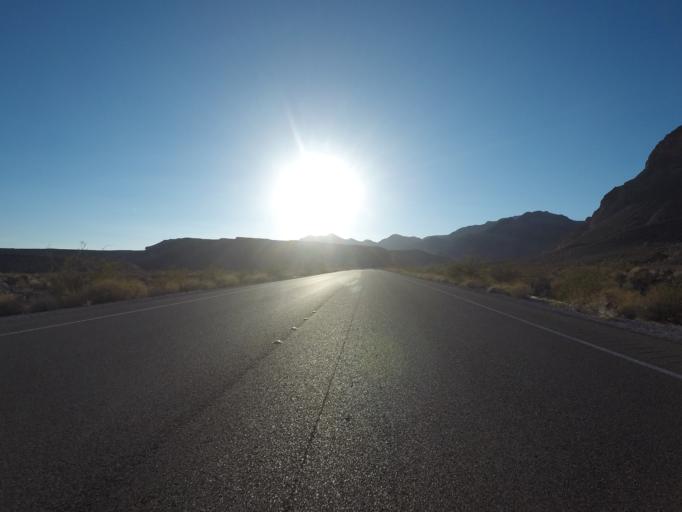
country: US
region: Nevada
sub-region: Clark County
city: Moapa Valley
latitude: 36.3647
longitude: -114.4644
